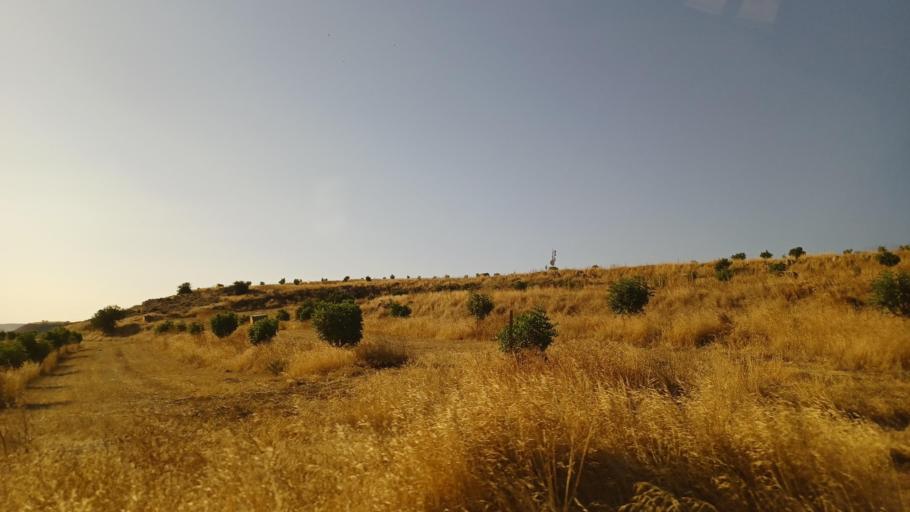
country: CY
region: Larnaka
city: Athienou
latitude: 35.0380
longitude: 33.5233
